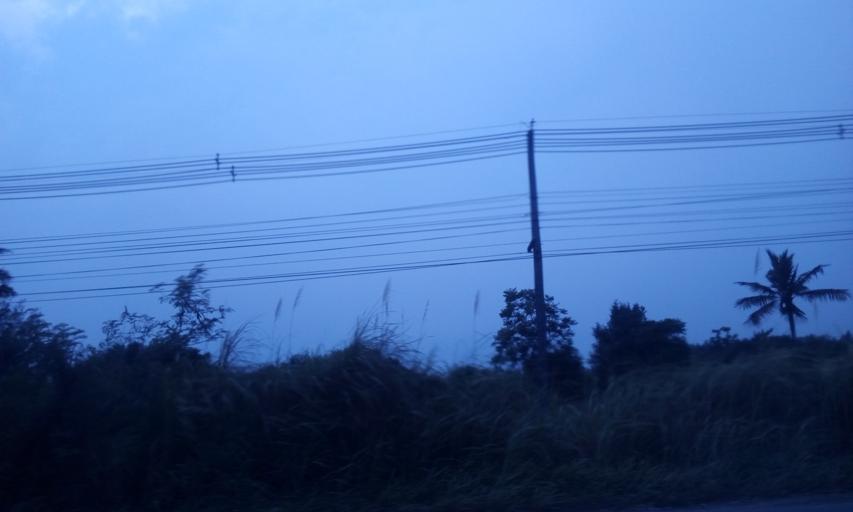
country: TH
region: Chon Buri
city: Ko Chan
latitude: 13.3050
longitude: 101.2635
